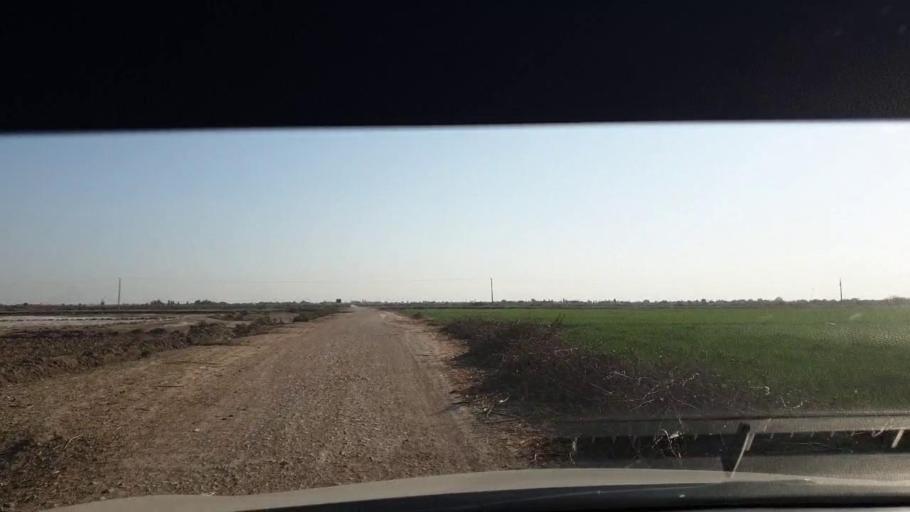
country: PK
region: Sindh
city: Berani
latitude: 25.7914
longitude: 68.9264
